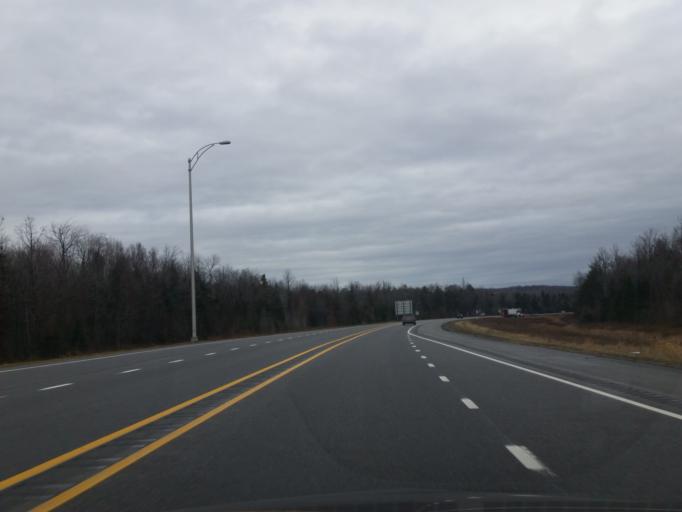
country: CA
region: Ontario
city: Clarence-Rockland
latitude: 45.6135
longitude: -75.3854
